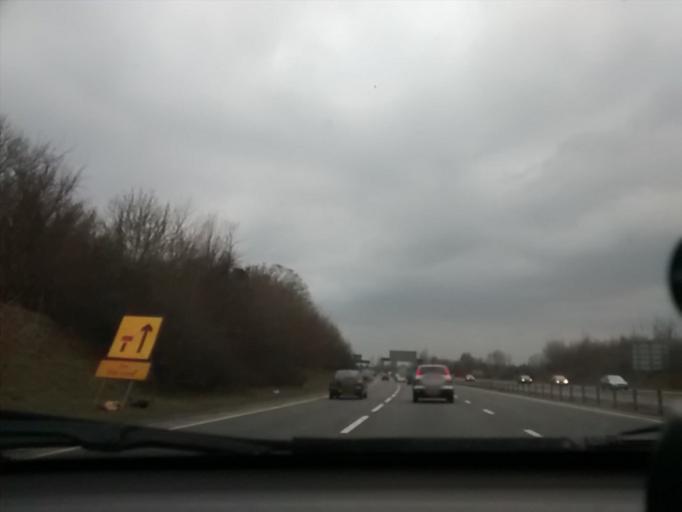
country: GB
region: England
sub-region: Cambridgeshire
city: Sawston
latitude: 52.1251
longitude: 0.2191
